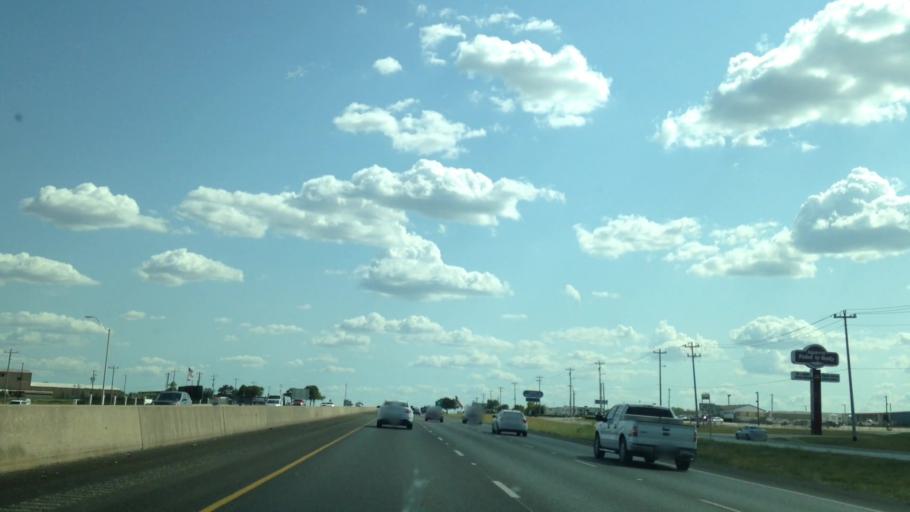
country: US
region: Texas
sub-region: Hays County
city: Buda
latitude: 30.0527
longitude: -97.8374
